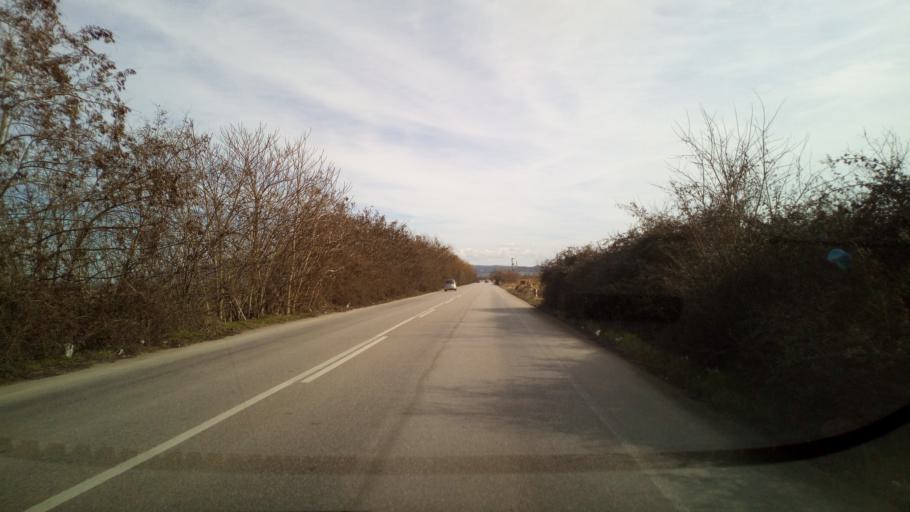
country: GR
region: Central Macedonia
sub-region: Nomos Thessalonikis
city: Gerakarou
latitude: 40.6507
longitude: 23.1687
